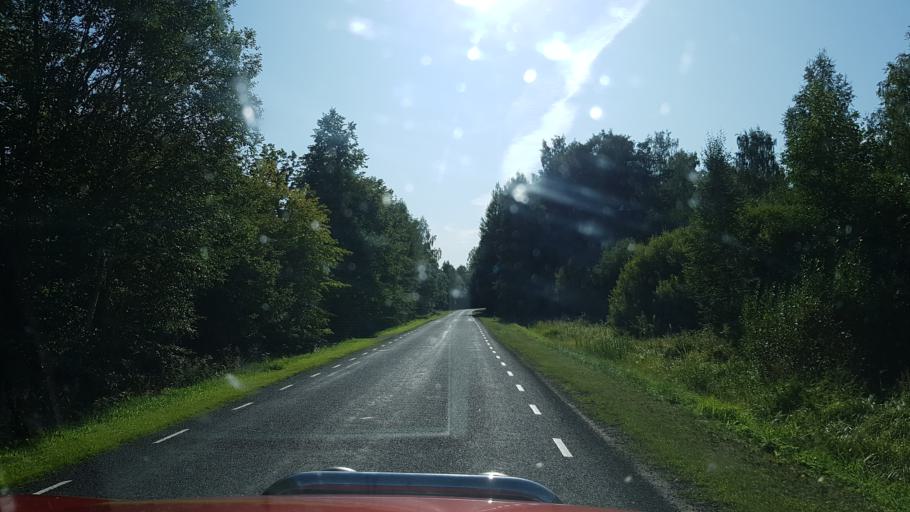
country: LV
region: Salacgrivas
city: Ainazi
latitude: 58.0766
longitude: 24.5192
